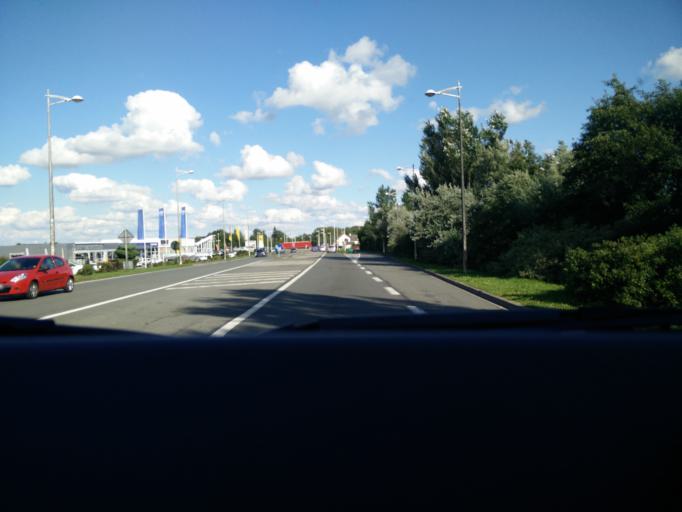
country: FR
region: Nord-Pas-de-Calais
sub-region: Departement du Nord
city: Feignies
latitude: 50.2805
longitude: 3.9052
